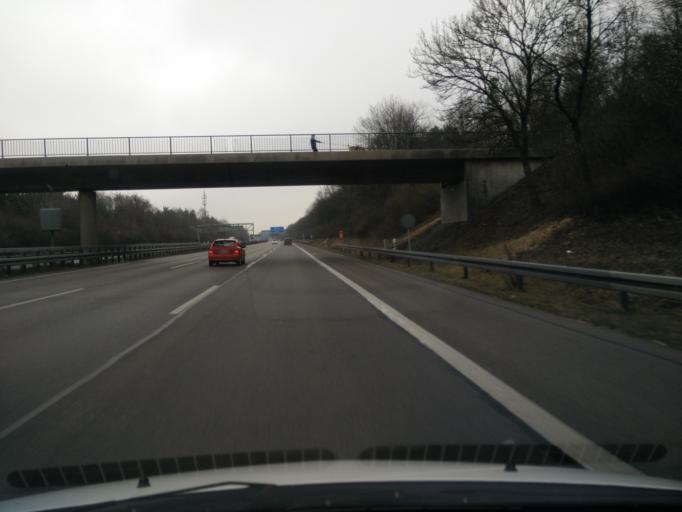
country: DE
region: Bavaria
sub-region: Upper Bavaria
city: Oberschleissheim
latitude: 48.2268
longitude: 11.5600
